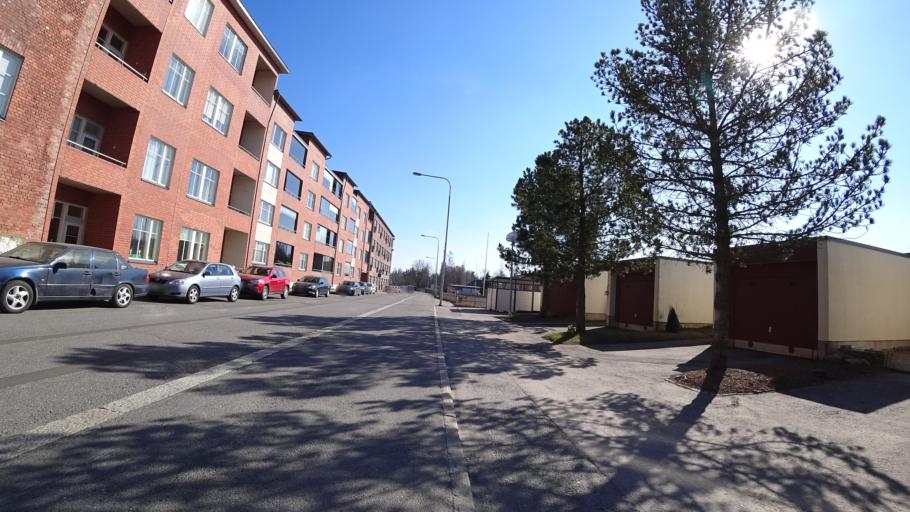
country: FI
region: Pirkanmaa
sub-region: Tampere
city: Pirkkala
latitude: 61.5094
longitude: 23.6625
